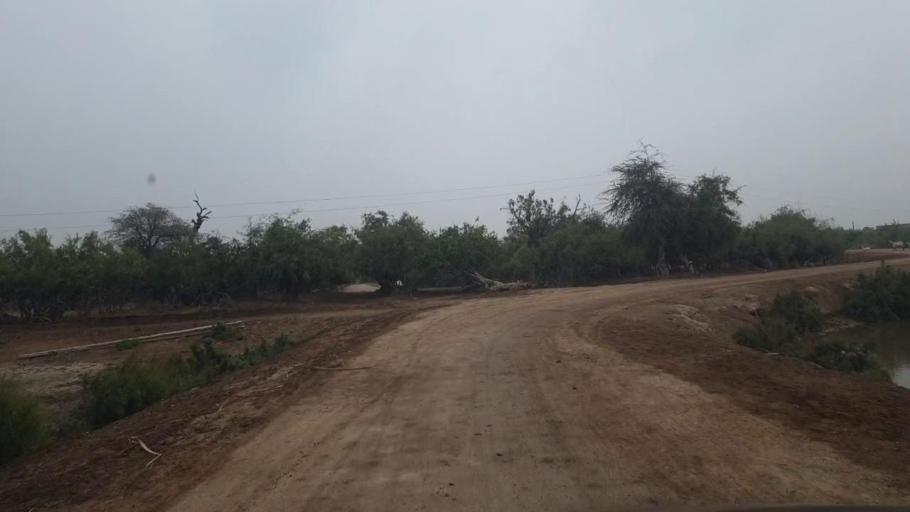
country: PK
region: Sindh
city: Tando Adam
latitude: 25.8319
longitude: 68.6973
